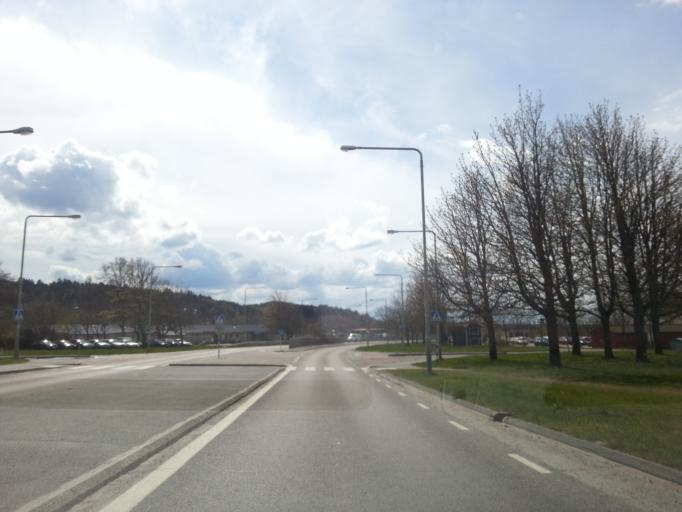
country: SE
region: Vaestra Goetaland
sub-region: Goteborg
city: Hammarkullen
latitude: 57.7700
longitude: 12.0278
